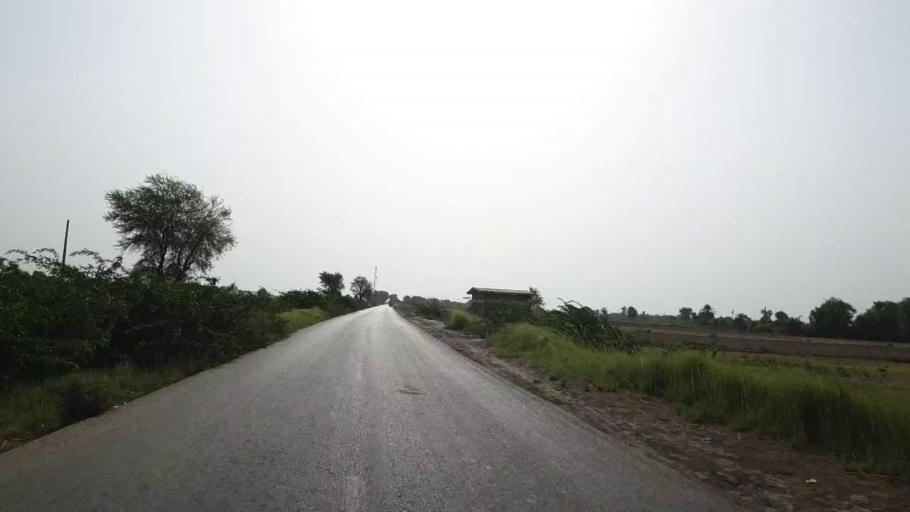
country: PK
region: Sindh
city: Nawabshah
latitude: 26.2674
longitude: 68.5157
